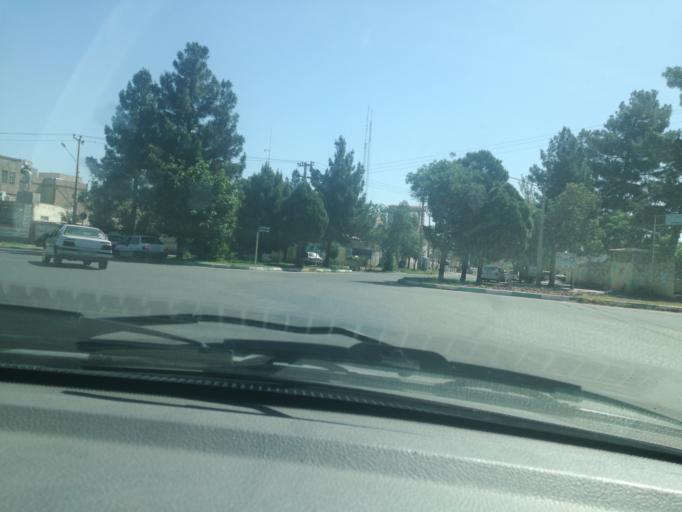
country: IR
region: Razavi Khorasan
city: Sarakhs
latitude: 36.5326
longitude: 61.1616
